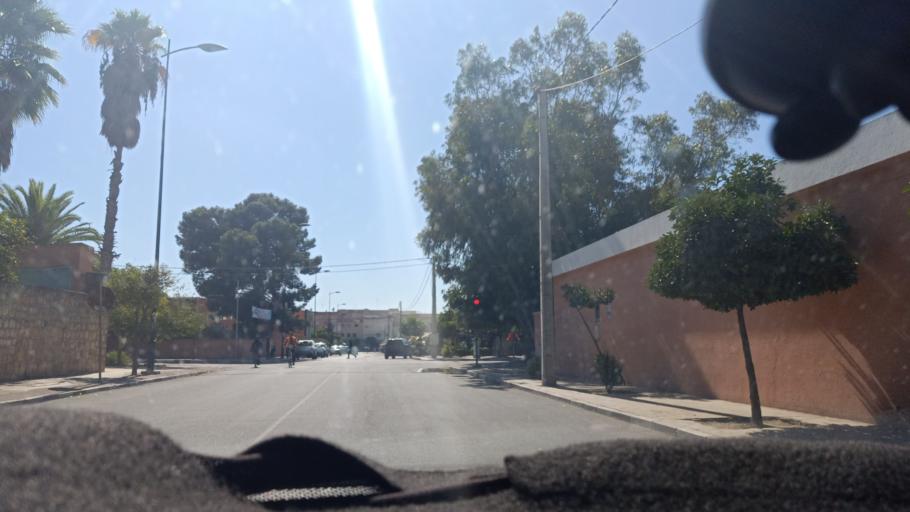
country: MA
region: Doukkala-Abda
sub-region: Safi
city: Youssoufia
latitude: 32.2437
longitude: -8.5343
